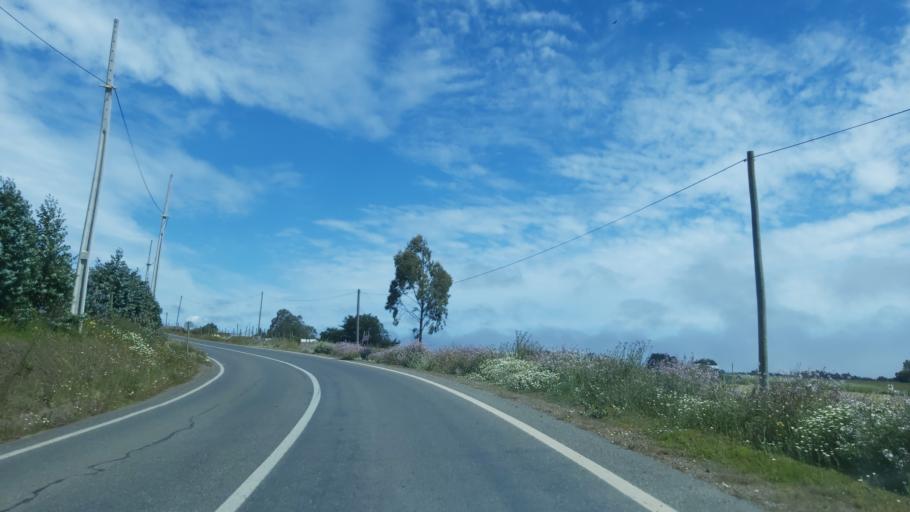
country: CL
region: Maule
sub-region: Provincia de Talca
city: Constitucion
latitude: -35.5755
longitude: -72.6029
